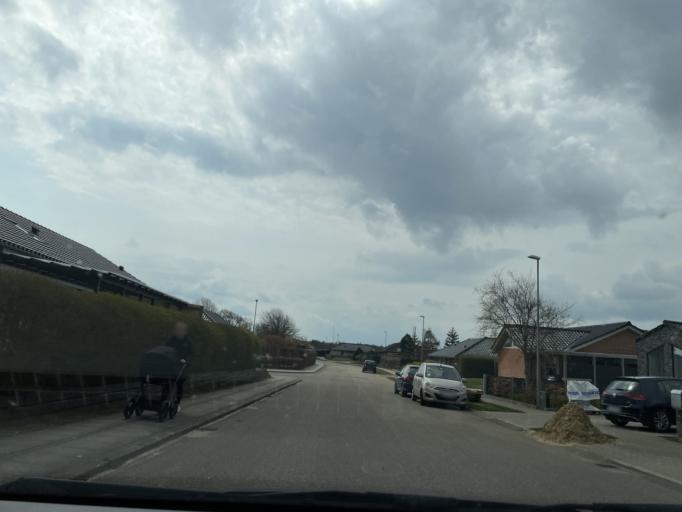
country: DK
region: South Denmark
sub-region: Esbjerg Kommune
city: Esbjerg
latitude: 55.4951
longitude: 8.4282
